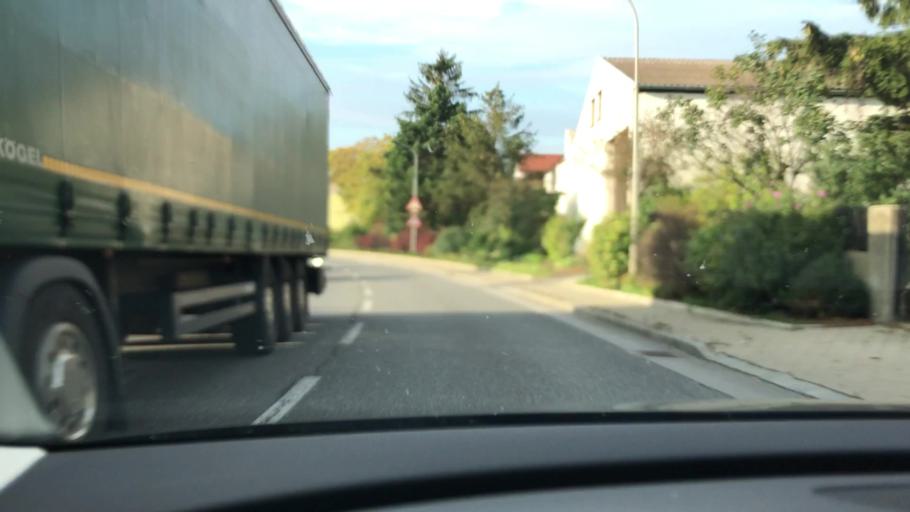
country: AT
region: Lower Austria
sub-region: Politischer Bezirk Mistelbach
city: Drasenhofen
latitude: 48.7539
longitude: 16.6479
